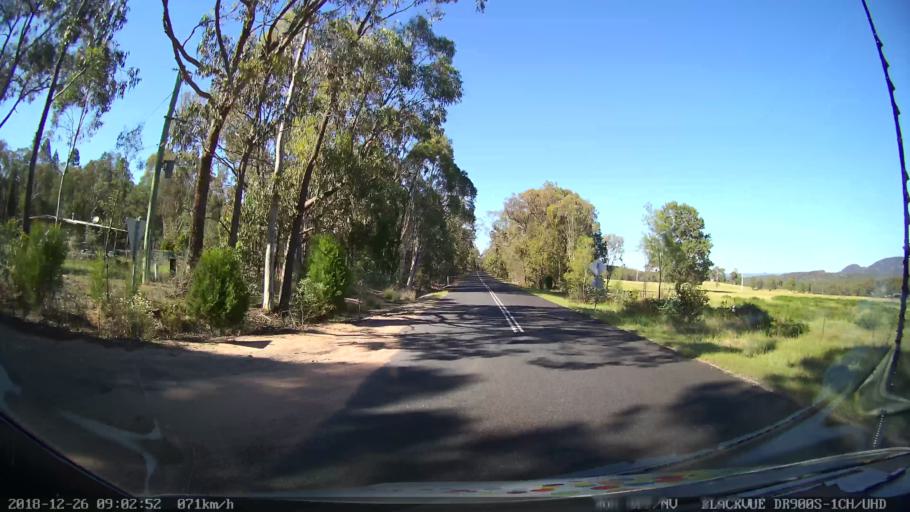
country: AU
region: New South Wales
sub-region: Mid-Western Regional
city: Kandos
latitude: -32.6572
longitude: 150.0168
